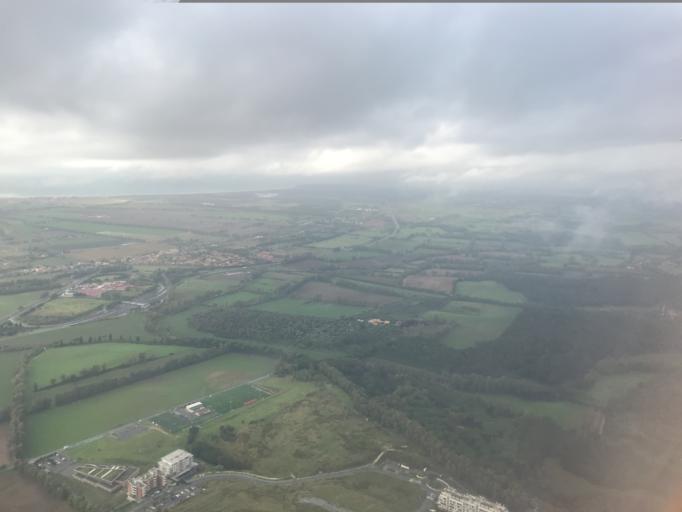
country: IT
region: Latium
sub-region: Citta metropolitana di Roma Capitale
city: Ara Nova
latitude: 41.9184
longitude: 12.2312
